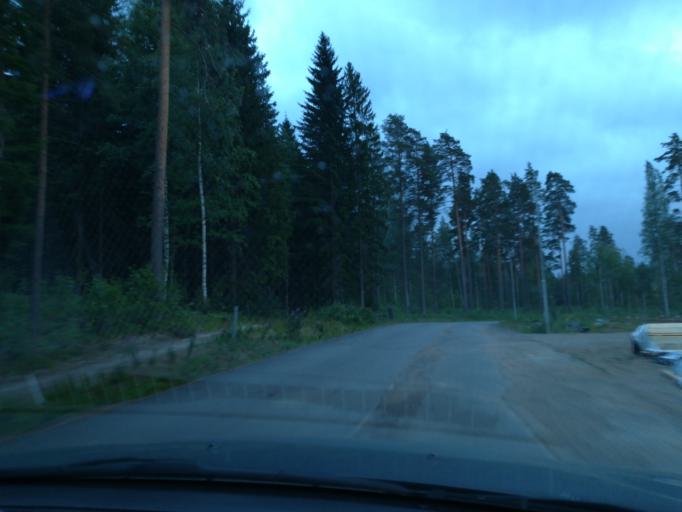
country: FI
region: Southern Savonia
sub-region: Mikkeli
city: Ristiina
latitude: 61.4924
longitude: 27.2738
